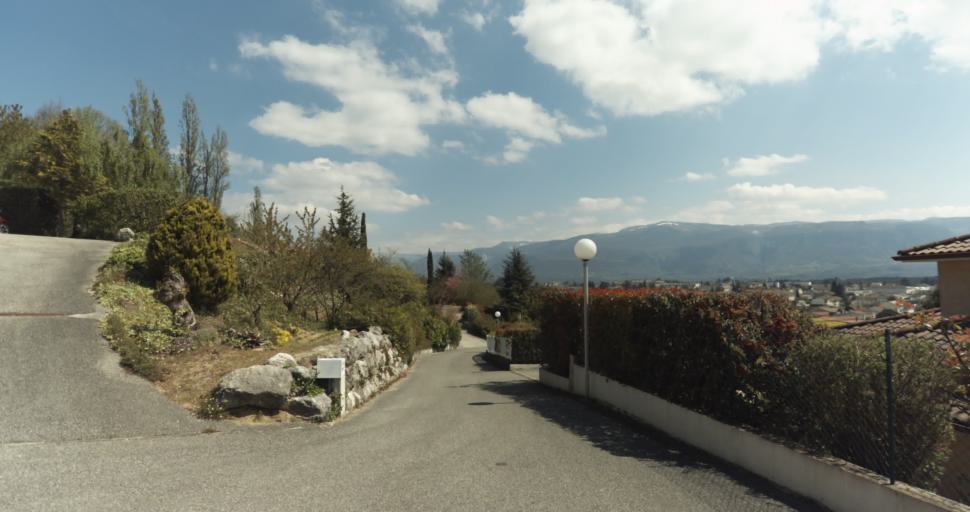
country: FR
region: Rhone-Alpes
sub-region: Departement de l'Isere
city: Saint-Marcellin
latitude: 45.1521
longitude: 5.3042
